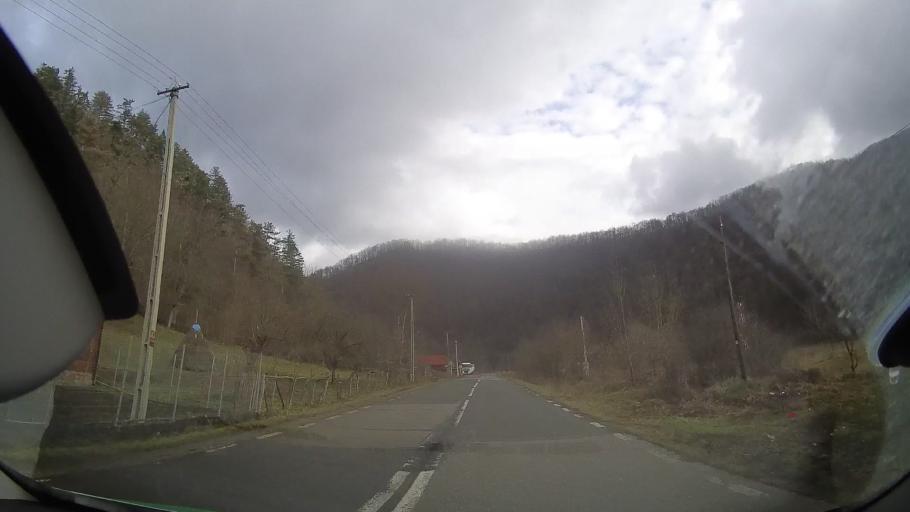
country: RO
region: Alba
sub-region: Comuna Rimetea
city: Rimetea
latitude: 46.5030
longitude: 23.5547
